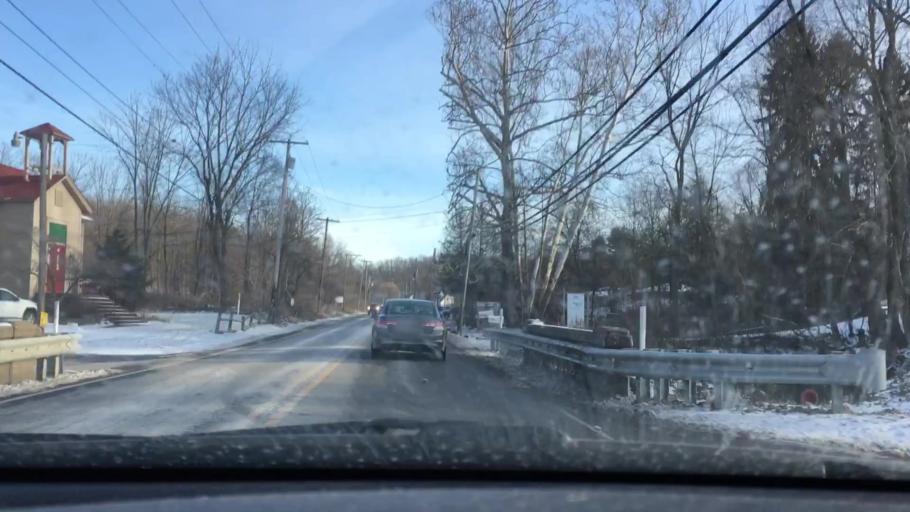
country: US
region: Pennsylvania
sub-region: Washington County
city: Thompsonville
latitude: 40.2718
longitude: -80.1246
